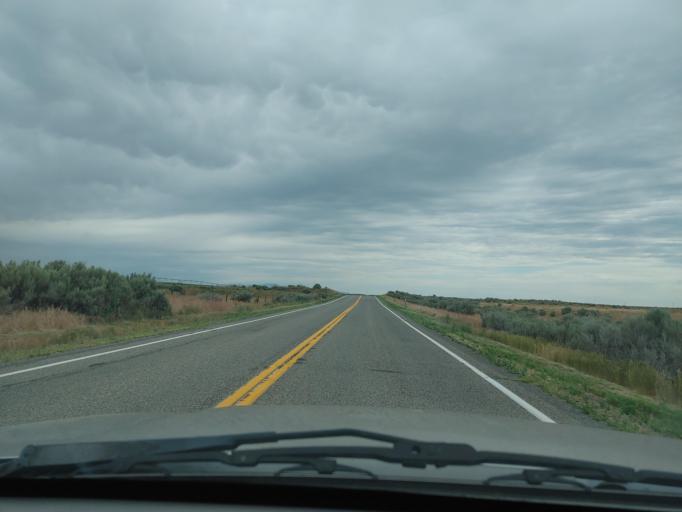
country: US
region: Idaho
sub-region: Lincoln County
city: Shoshone
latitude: 43.0594
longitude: -114.1291
